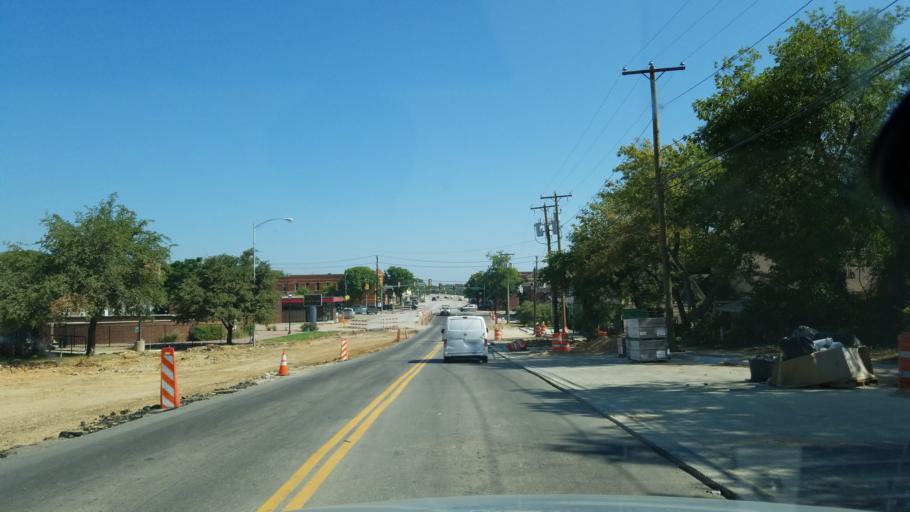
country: US
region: Texas
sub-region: Tarrant County
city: Mansfield
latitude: 32.5619
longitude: -97.1422
